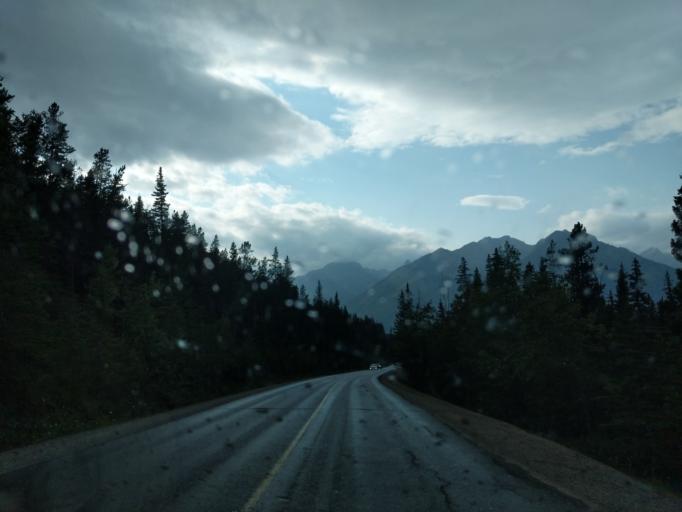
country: CA
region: Alberta
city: Banff
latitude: 51.1605
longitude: -115.5684
